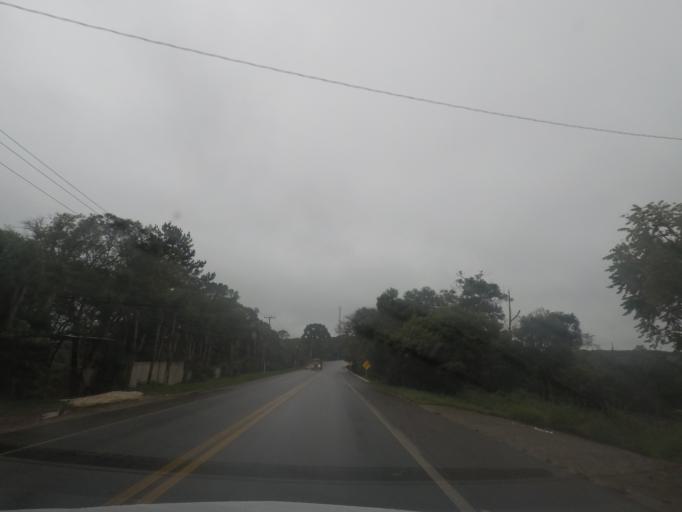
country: BR
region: Parana
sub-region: Colombo
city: Colombo
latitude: -25.3141
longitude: -49.1510
